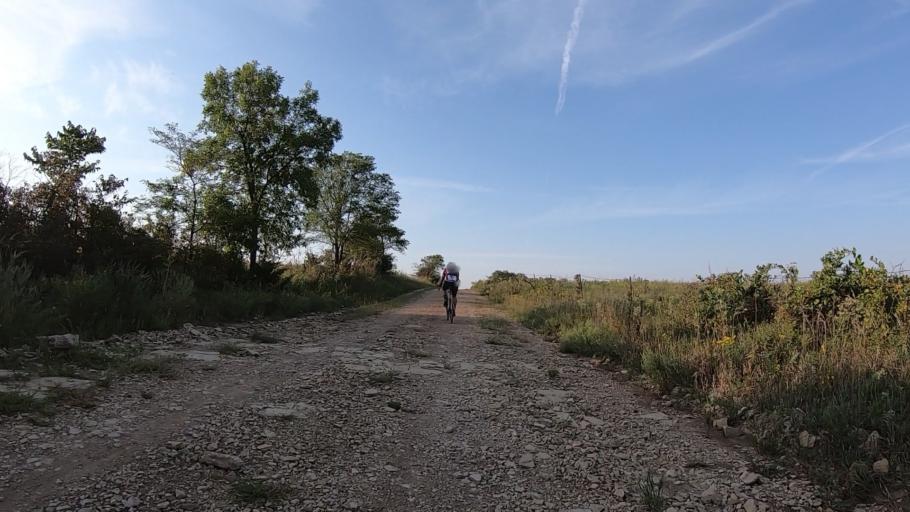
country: US
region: Kansas
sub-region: Marshall County
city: Blue Rapids
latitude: 39.7531
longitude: -96.7506
